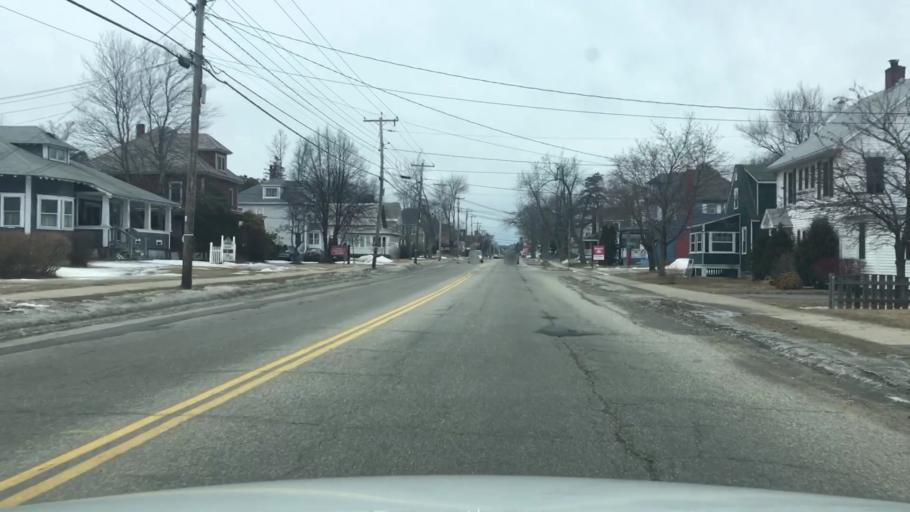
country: US
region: Maine
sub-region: York County
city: Sanford (historical)
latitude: 43.4292
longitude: -70.7681
